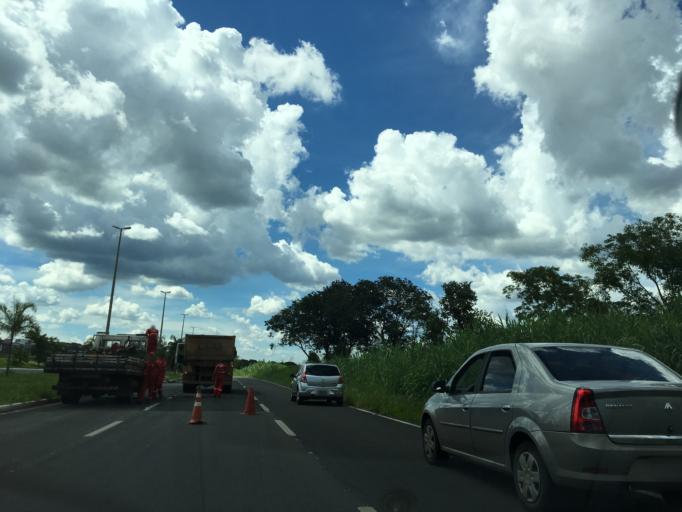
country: BR
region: Federal District
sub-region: Brasilia
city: Brasilia
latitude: -15.7479
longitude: -47.8796
